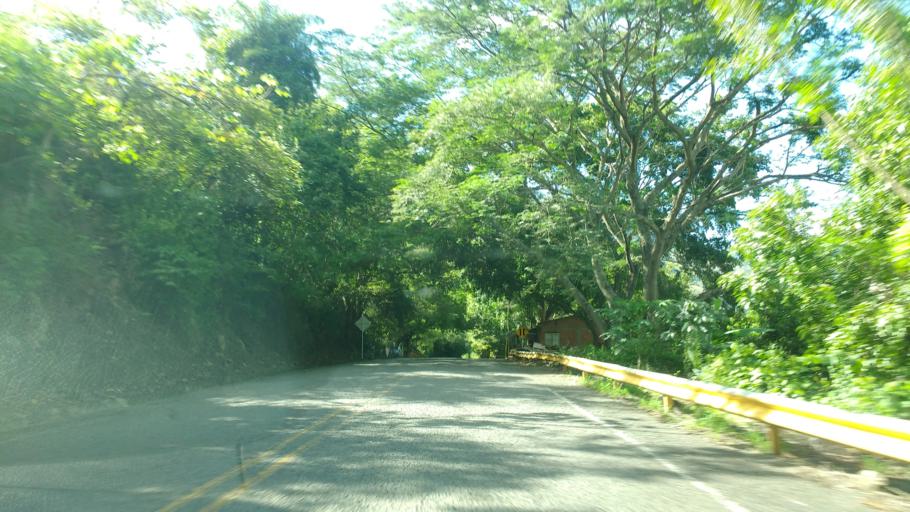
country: CO
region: Antioquia
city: Concordia
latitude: 6.0367
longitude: -75.8574
